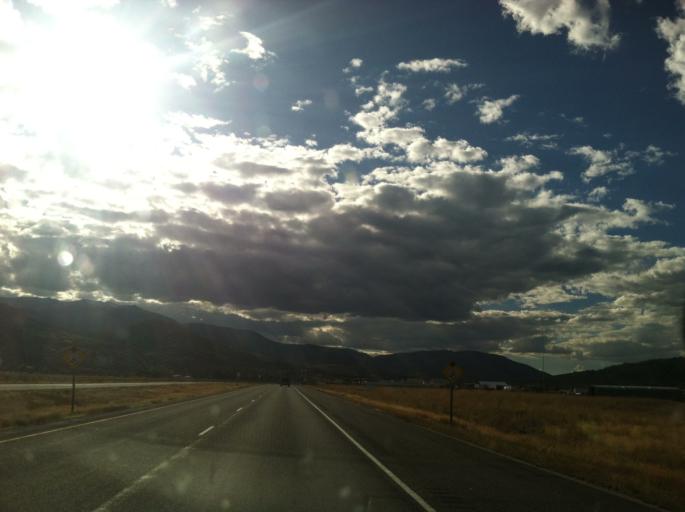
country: US
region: Montana
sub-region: Deer Lodge County
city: Anaconda
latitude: 46.1271
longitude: -112.9173
